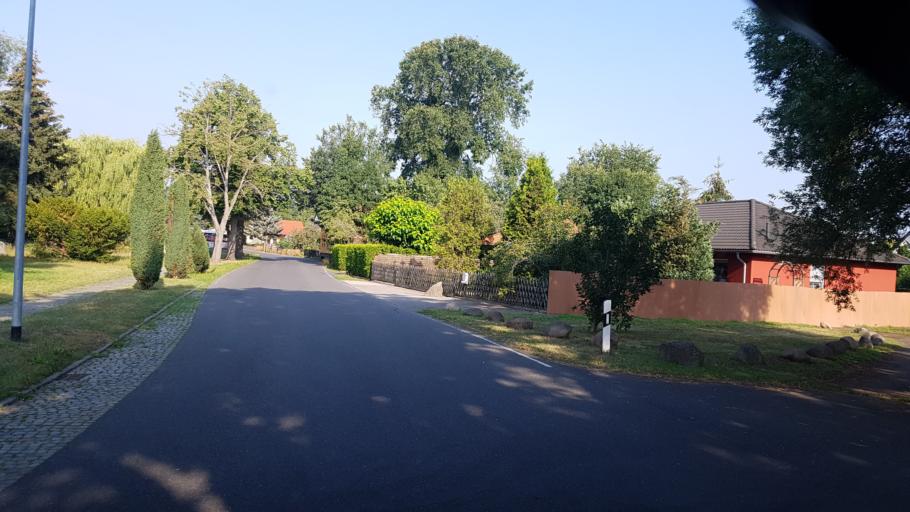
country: DE
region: Brandenburg
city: Drebkau
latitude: 51.6718
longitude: 14.2324
